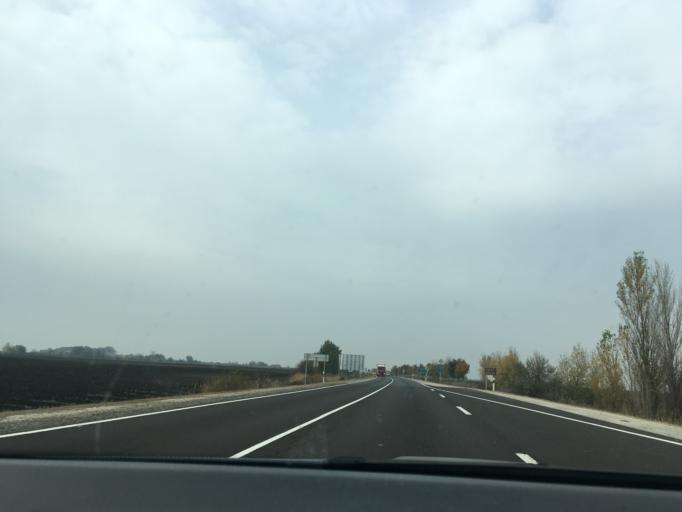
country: HU
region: Jasz-Nagykun-Szolnok
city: Zagyvarekas
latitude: 47.1847
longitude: 20.0972
